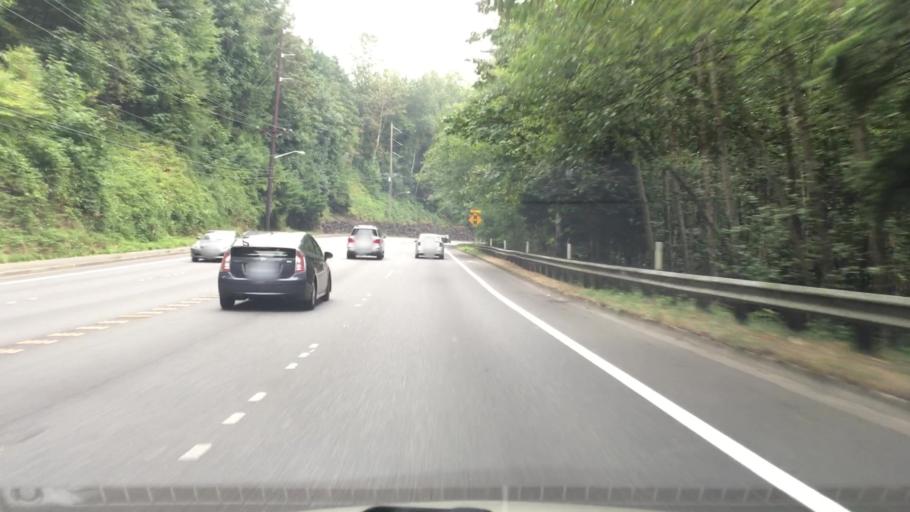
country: US
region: Washington
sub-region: King County
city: Newport
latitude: 47.5587
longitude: -122.1680
